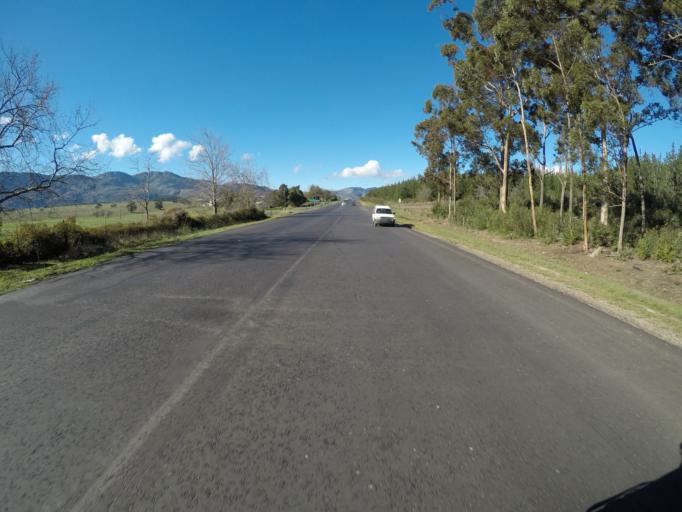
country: ZA
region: Western Cape
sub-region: Overberg District Municipality
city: Grabouw
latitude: -34.1779
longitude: 19.0644
